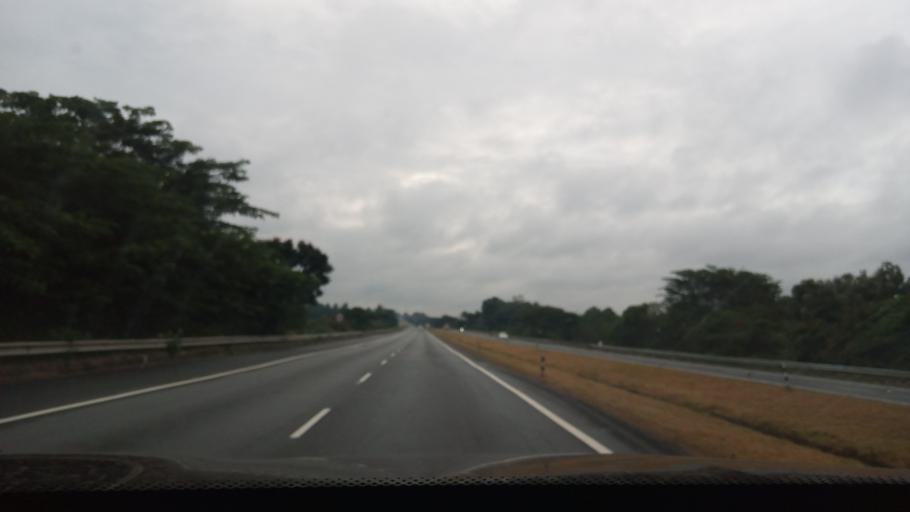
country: IN
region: Karnataka
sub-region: Bangalore Urban
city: Bangalore
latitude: 12.9421
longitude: 77.4698
